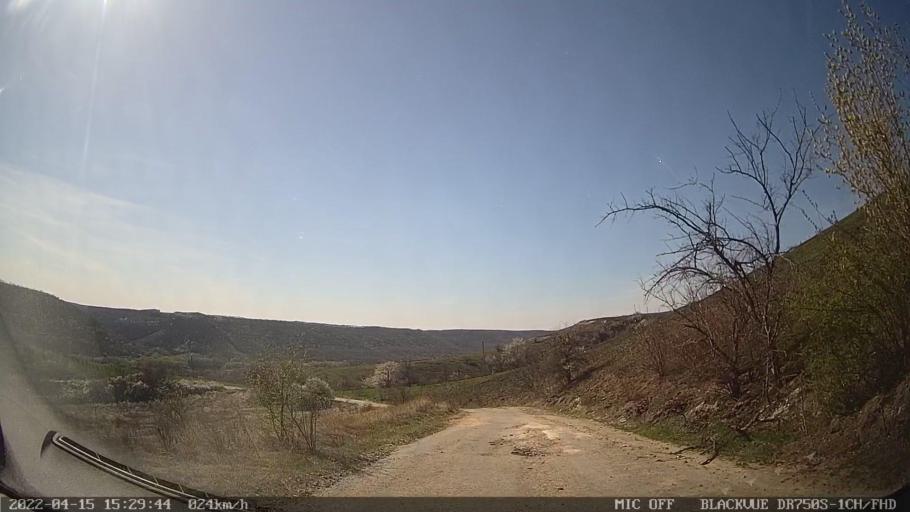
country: MD
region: Raionul Ocnita
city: Otaci
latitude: 48.3554
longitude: 27.9243
